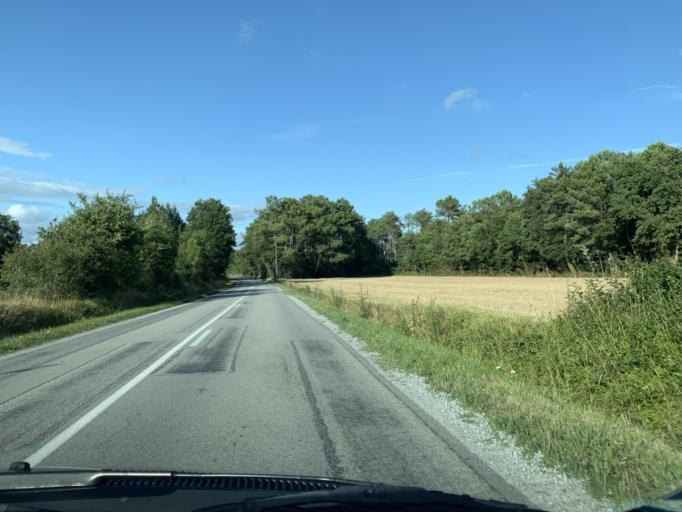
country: FR
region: Brittany
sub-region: Departement du Morbihan
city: Ferel
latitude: 47.4942
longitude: -2.3258
